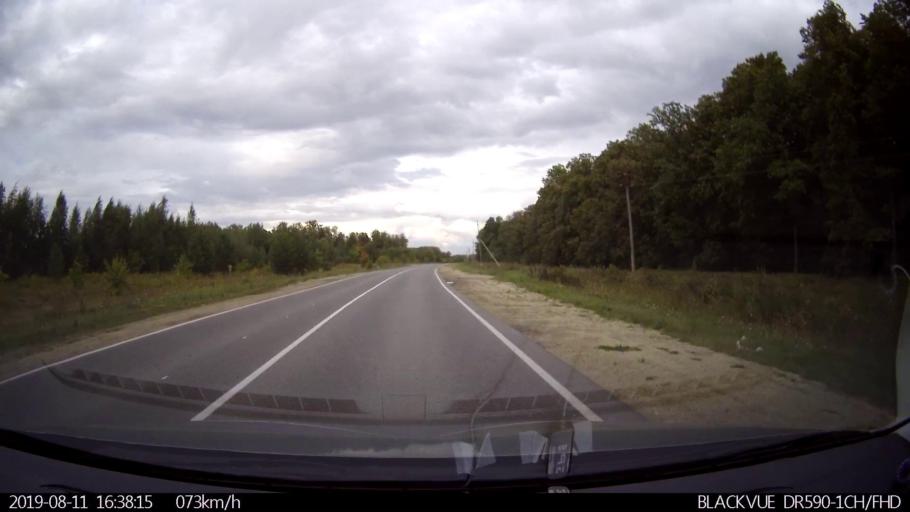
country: RU
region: Ulyanovsk
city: Mayna
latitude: 54.1338
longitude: 47.6230
